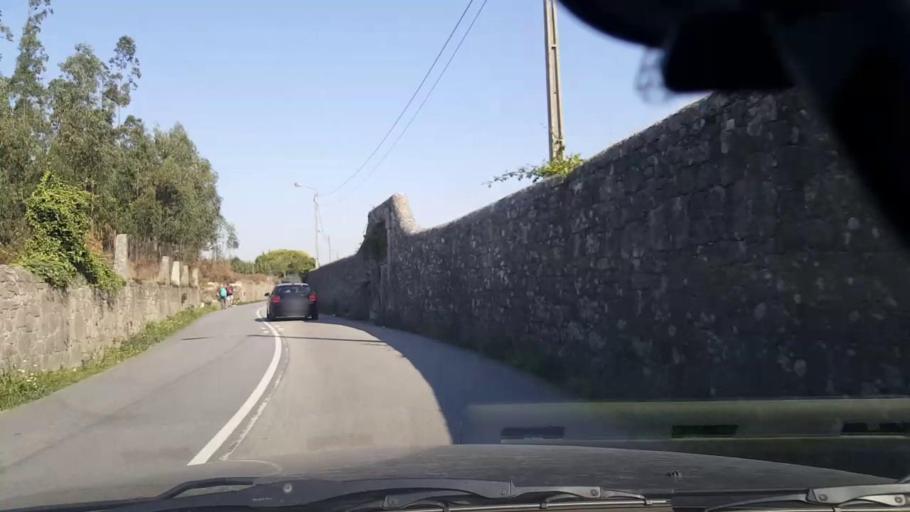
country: PT
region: Porto
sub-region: Vila do Conde
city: Arvore
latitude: 41.3305
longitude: -8.6803
